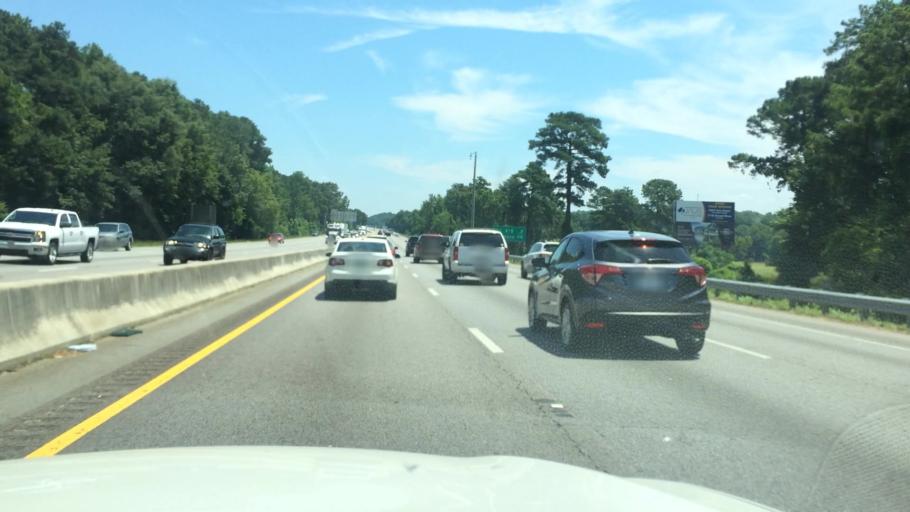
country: US
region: South Carolina
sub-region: Lexington County
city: Saint Andrews
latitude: 34.0452
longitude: -81.0798
